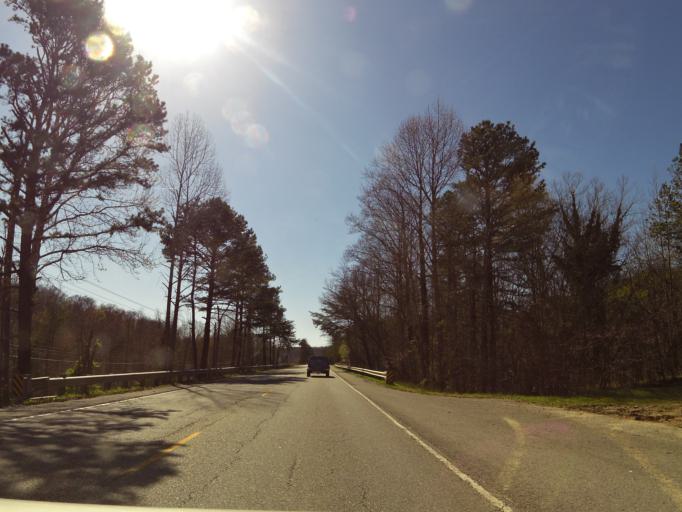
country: US
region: Tennessee
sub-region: Scott County
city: Oneida
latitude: 36.5376
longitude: -84.4726
